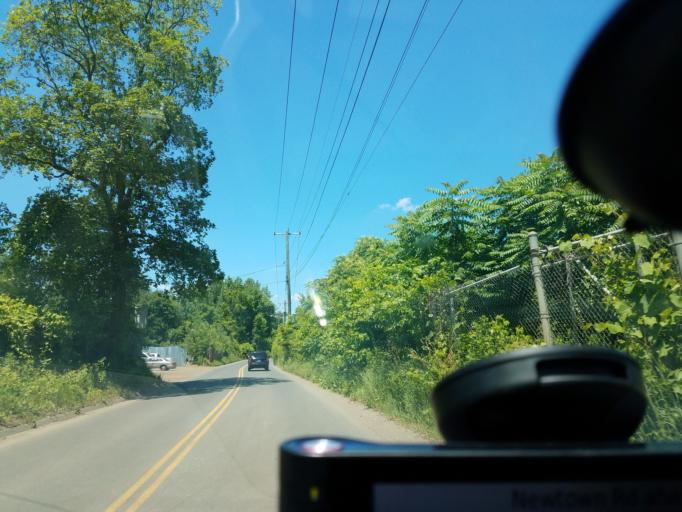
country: US
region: Connecticut
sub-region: Fairfield County
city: Bethel
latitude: 41.3994
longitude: -73.4140
